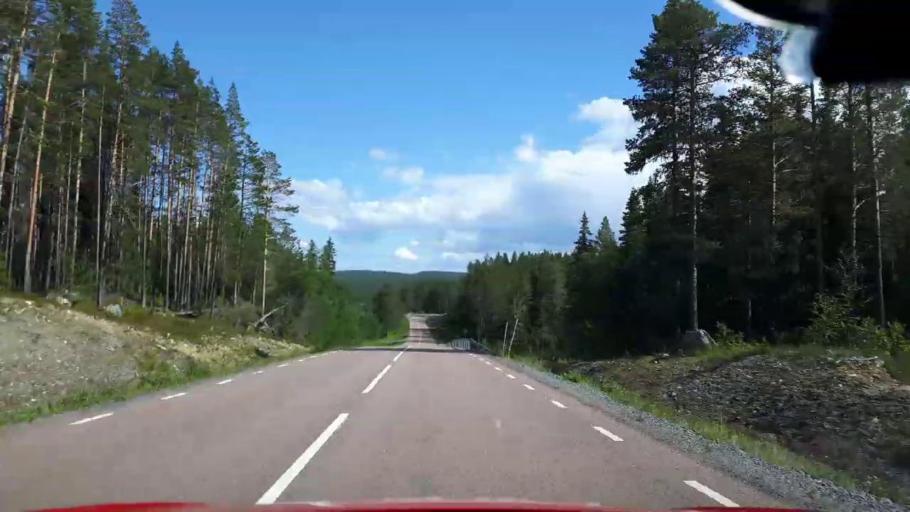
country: SE
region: Jaemtland
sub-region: Krokoms Kommun
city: Valla
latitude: 64.0125
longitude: 14.2260
